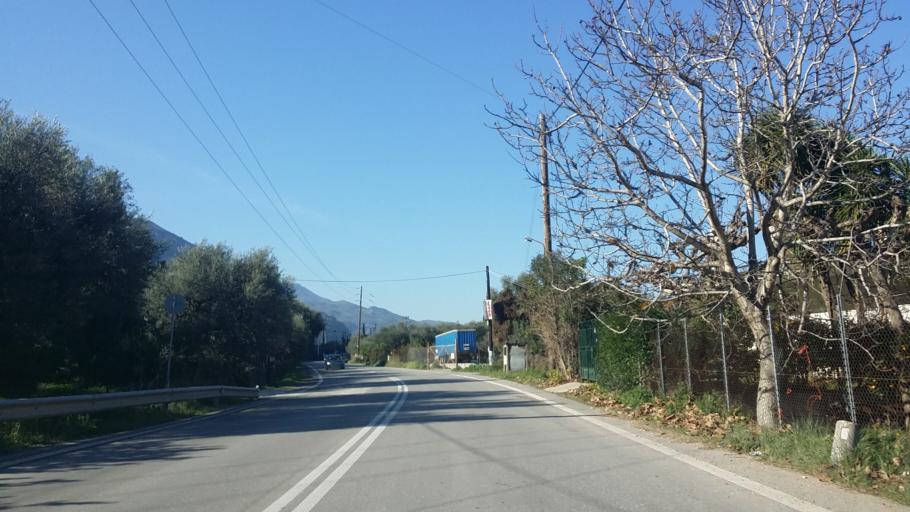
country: GR
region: West Greece
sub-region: Nomos Achaias
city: Temeni
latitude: 38.1829
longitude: 22.2067
